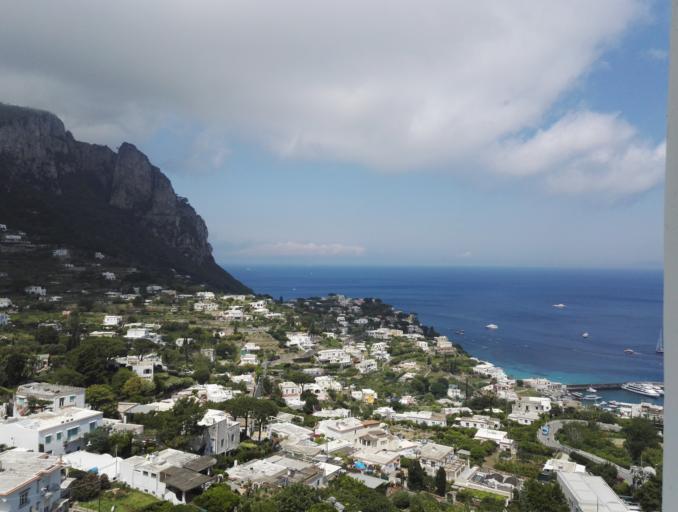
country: IT
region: Campania
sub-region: Provincia di Napoli
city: Capri
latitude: 40.5510
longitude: 14.2427
